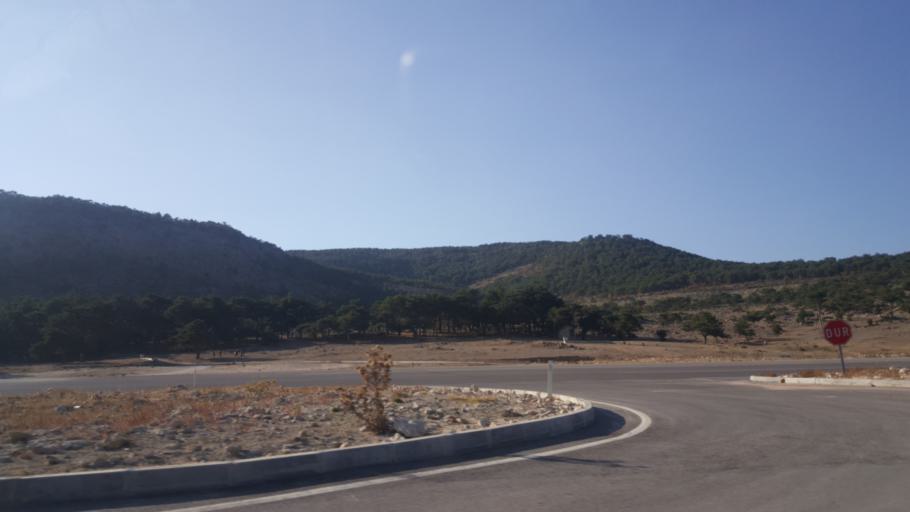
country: TR
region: Afyonkarahisar
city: Ihsaniye
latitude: 39.0969
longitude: 30.5761
